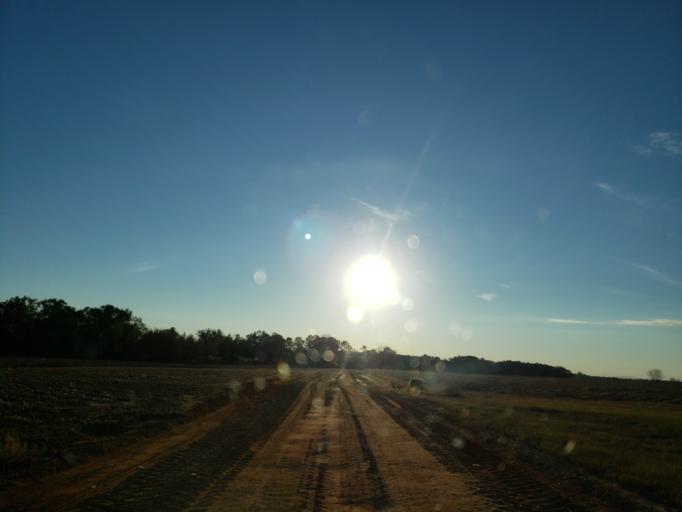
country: US
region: Georgia
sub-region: Dooly County
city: Vienna
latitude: 32.1431
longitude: -83.7426
